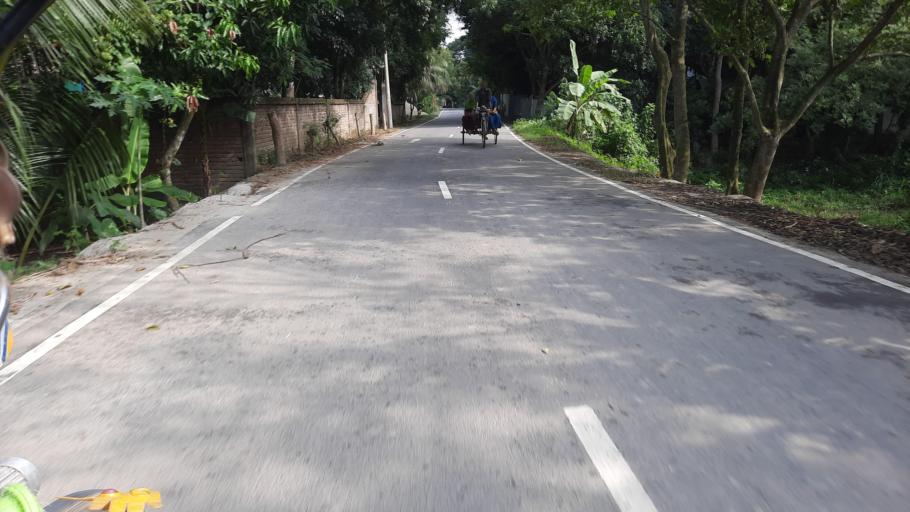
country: BD
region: Khulna
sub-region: Magura
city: Magura
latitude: 23.4540
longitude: 89.6120
